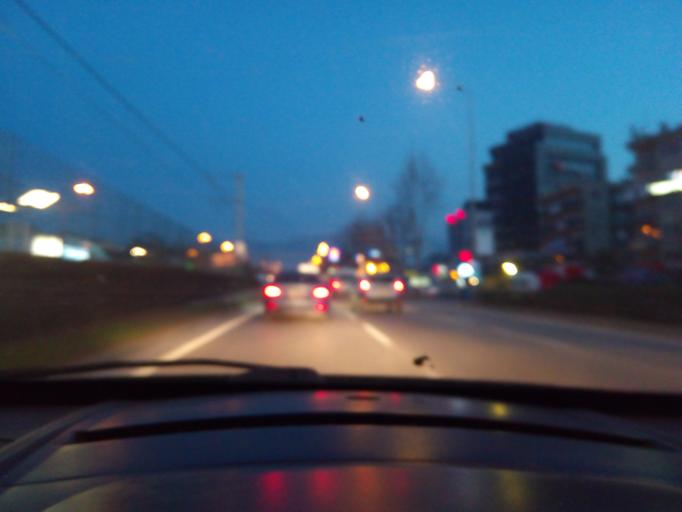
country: TR
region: Bursa
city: Niluefer
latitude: 40.2367
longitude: 28.9757
